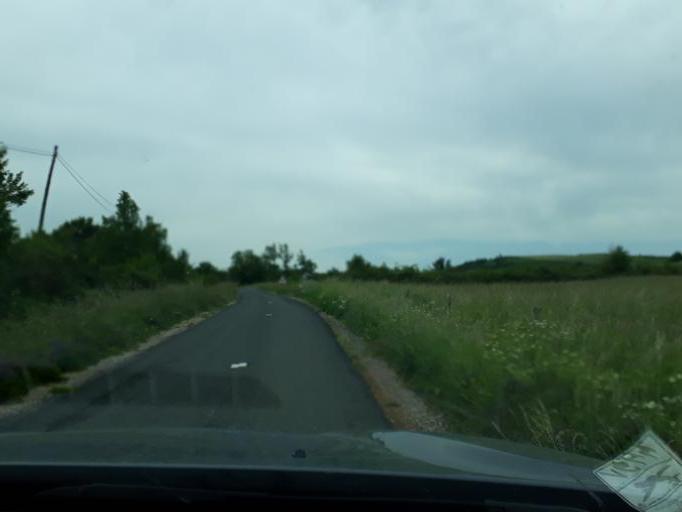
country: FR
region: Languedoc-Roussillon
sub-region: Departement de l'Herault
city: Lodeve
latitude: 43.8326
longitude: 3.2752
